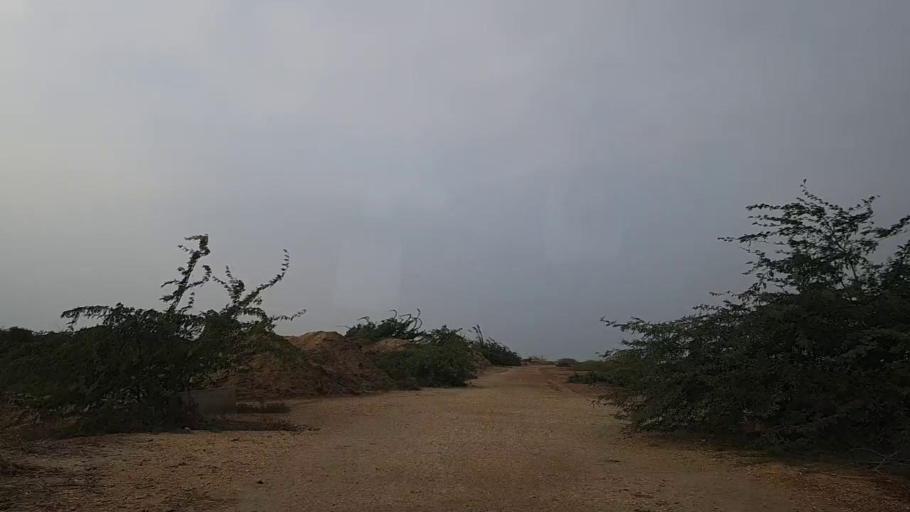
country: PK
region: Sindh
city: Mirpur Sakro
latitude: 24.6090
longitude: 67.5156
